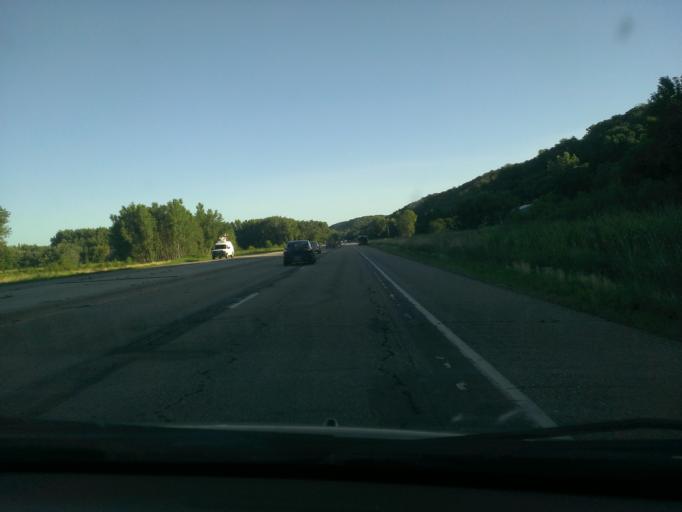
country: US
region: Minnesota
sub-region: Nicollet County
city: North Mankato
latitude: 44.2294
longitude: -94.0274
